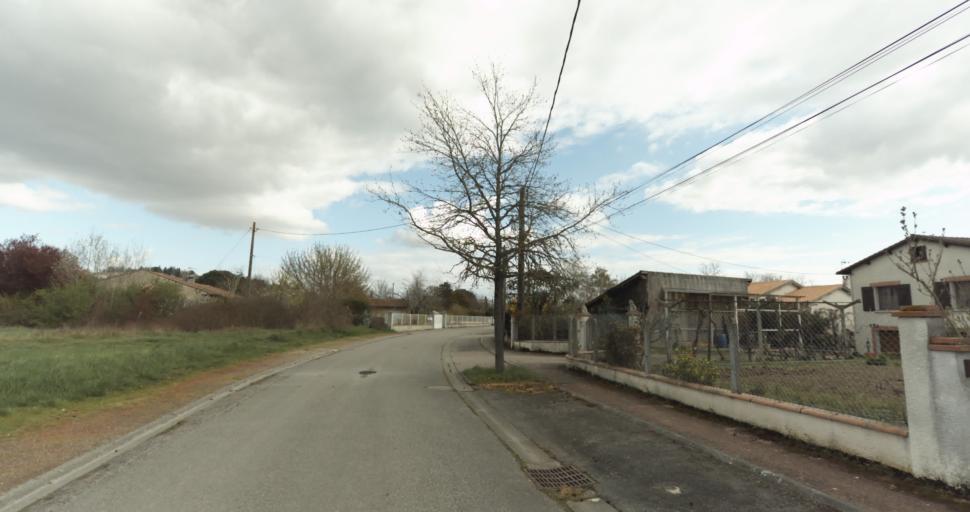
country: FR
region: Midi-Pyrenees
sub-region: Departement de la Haute-Garonne
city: Auterive
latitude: 43.3408
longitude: 1.4879
